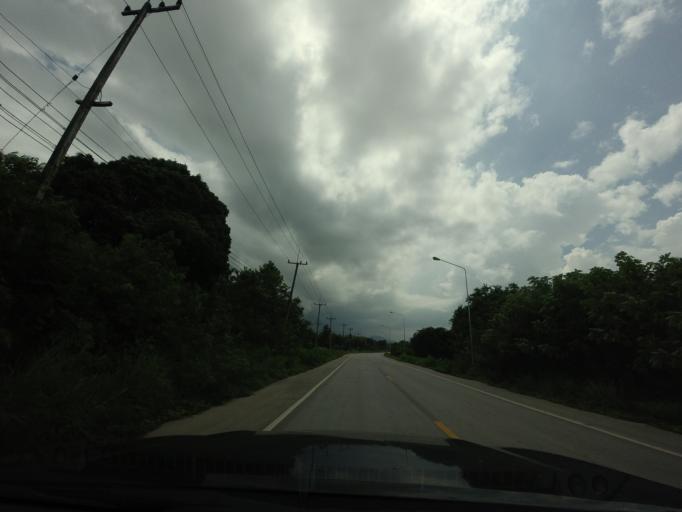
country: TH
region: Loei
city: Pak Chom
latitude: 18.0248
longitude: 101.7651
